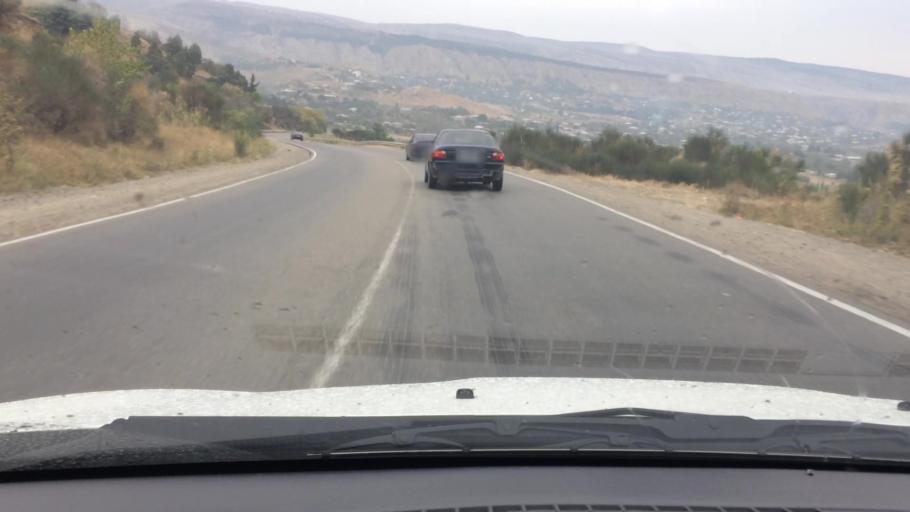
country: GE
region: T'bilisi
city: Tbilisi
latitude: 41.5935
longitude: 44.7807
